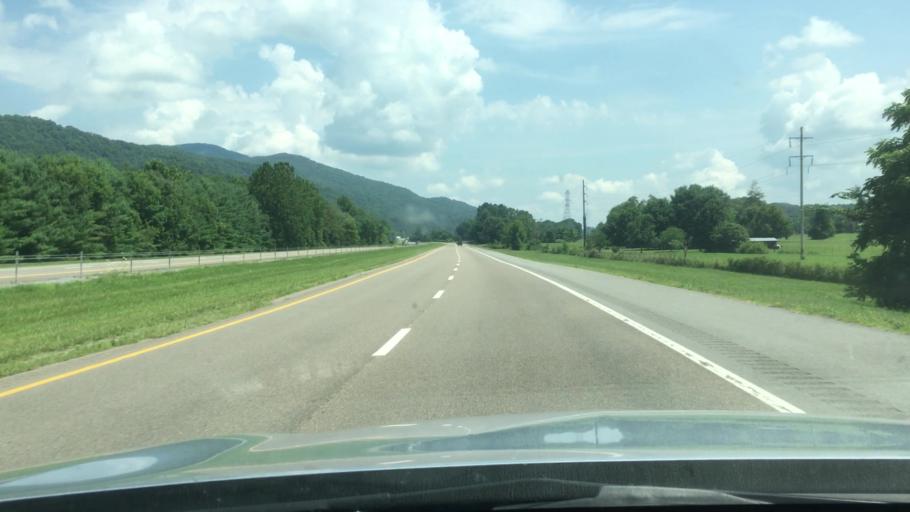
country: US
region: Tennessee
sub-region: Unicoi County
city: Erwin
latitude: 36.1738
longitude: -82.3862
